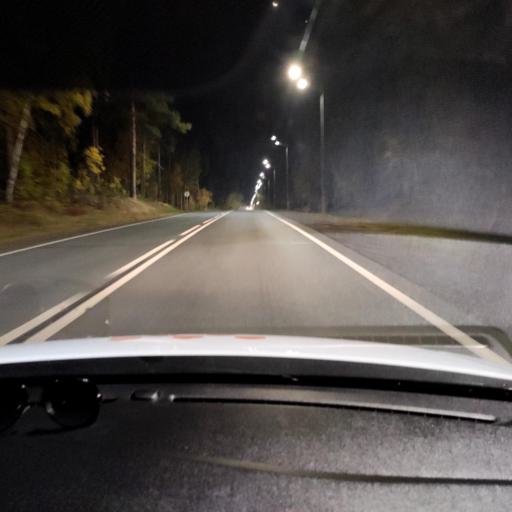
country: RU
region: Tatarstan
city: Verkhniy Uslon
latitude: 55.6384
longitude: 49.0416
